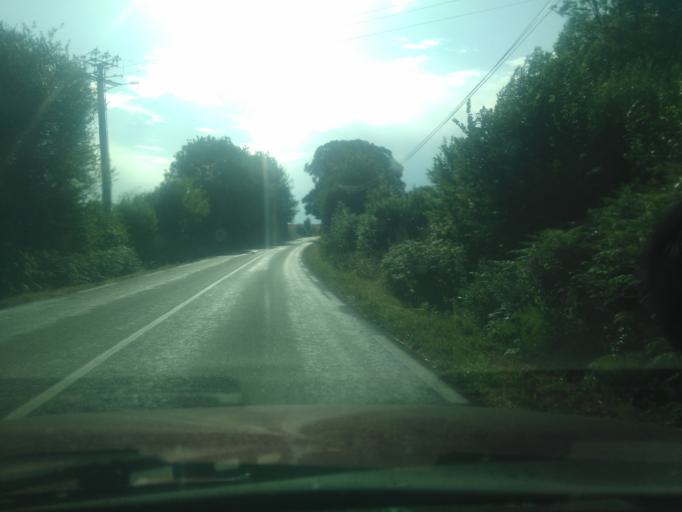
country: FR
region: Pays de la Loire
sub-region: Departement de la Vendee
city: Saint-Pierre-du-Chemin
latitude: 46.6518
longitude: -0.6653
